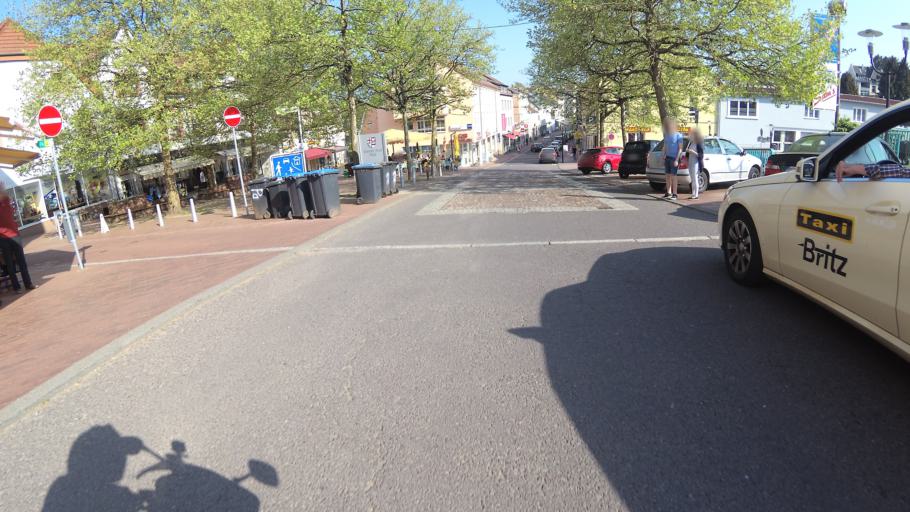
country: DE
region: Saarland
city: Illingen
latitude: 49.3776
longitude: 7.0507
